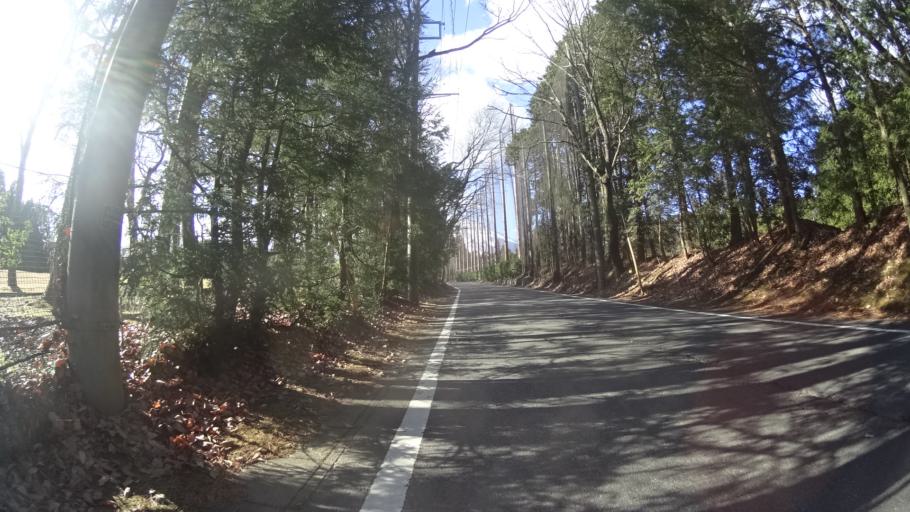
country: JP
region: Shizuoka
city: Gotemba
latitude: 35.3442
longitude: 138.8921
